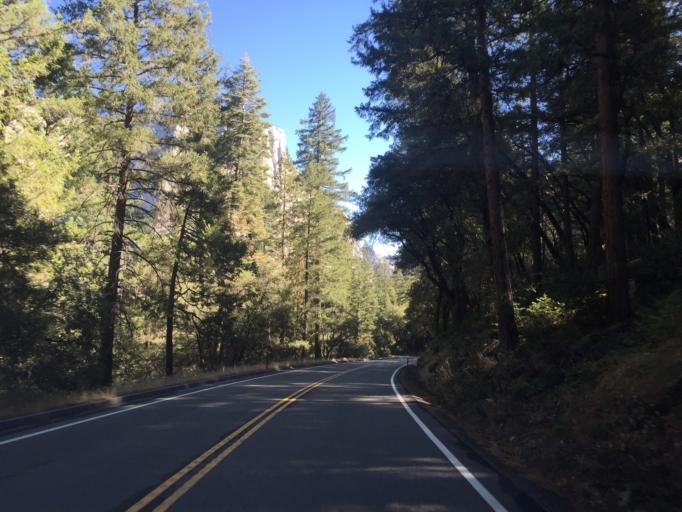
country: US
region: California
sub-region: Mariposa County
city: Yosemite Valley
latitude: 37.7135
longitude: -119.6598
